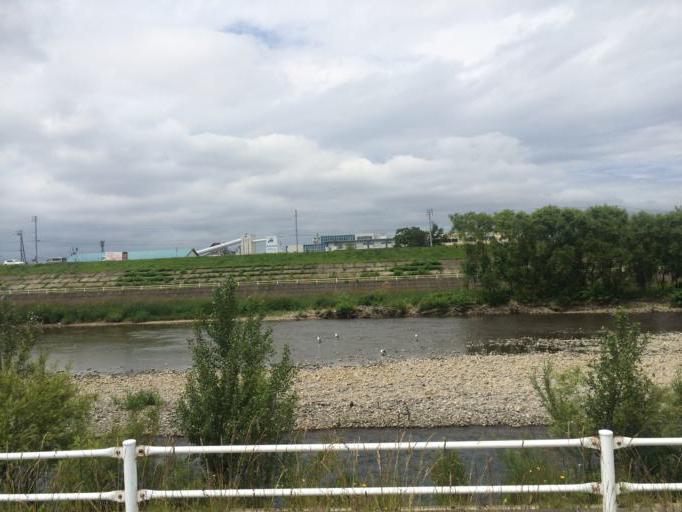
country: JP
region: Hokkaido
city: Sapporo
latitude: 43.0673
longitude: 141.3881
